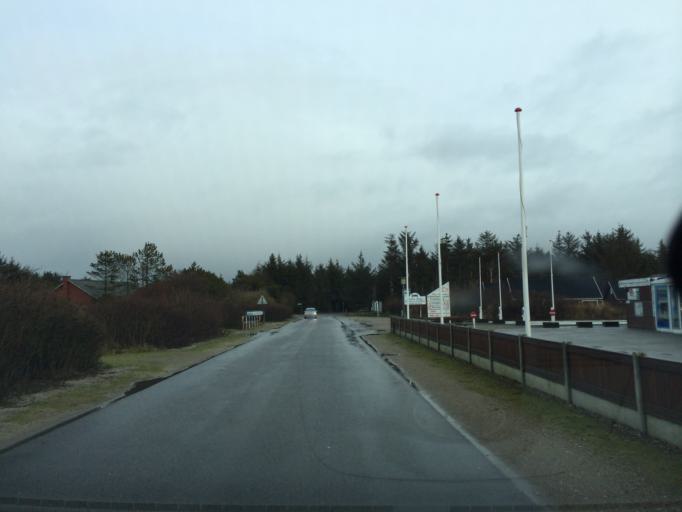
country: DK
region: Central Jutland
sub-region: Holstebro Kommune
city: Ulfborg
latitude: 56.2597
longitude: 8.1453
